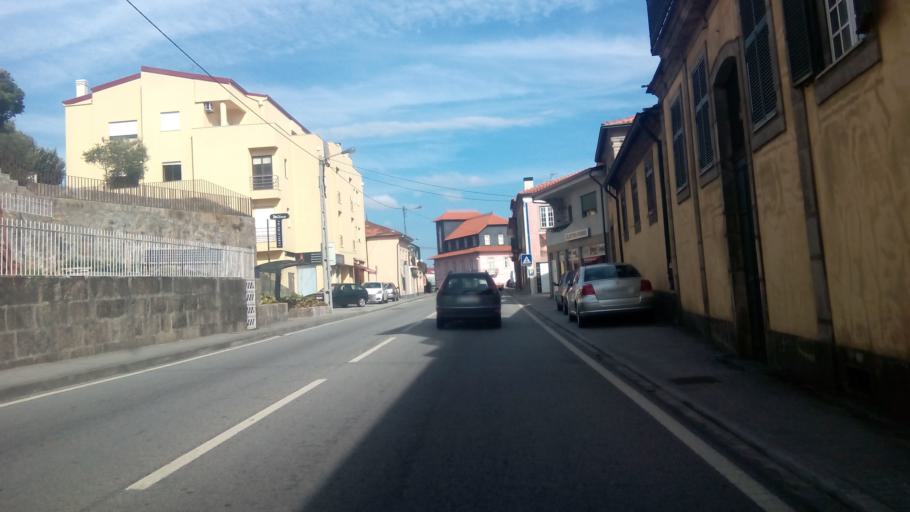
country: PT
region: Porto
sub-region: Paredes
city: Baltar
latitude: 41.1922
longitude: -8.3910
